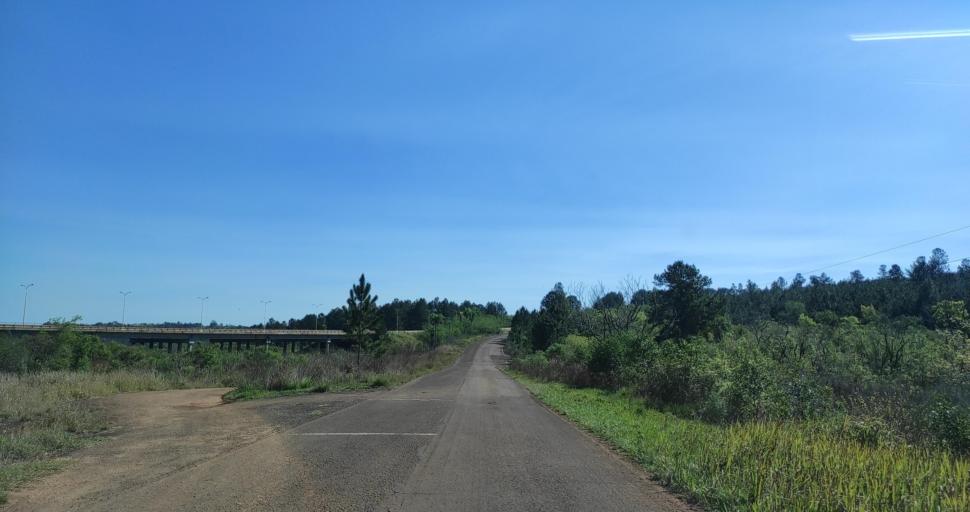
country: AR
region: Misiones
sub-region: Departamento de Candelaria
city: Loreto
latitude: -27.3065
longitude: -55.5385
